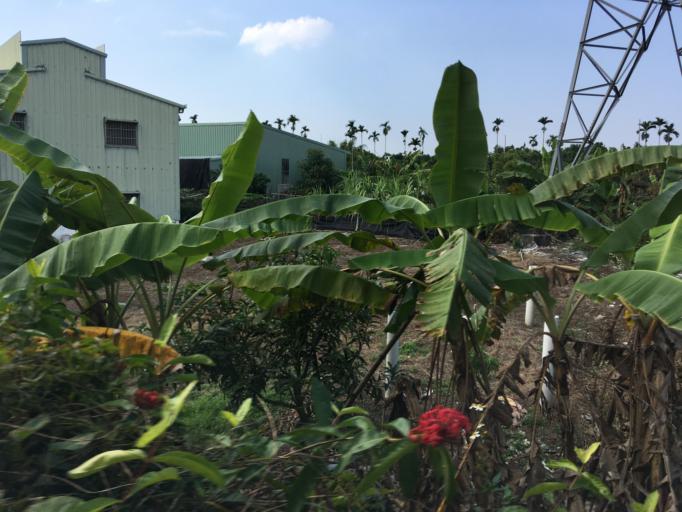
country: TW
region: Taiwan
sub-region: Chiayi
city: Jiayi Shi
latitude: 23.4931
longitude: 120.5215
